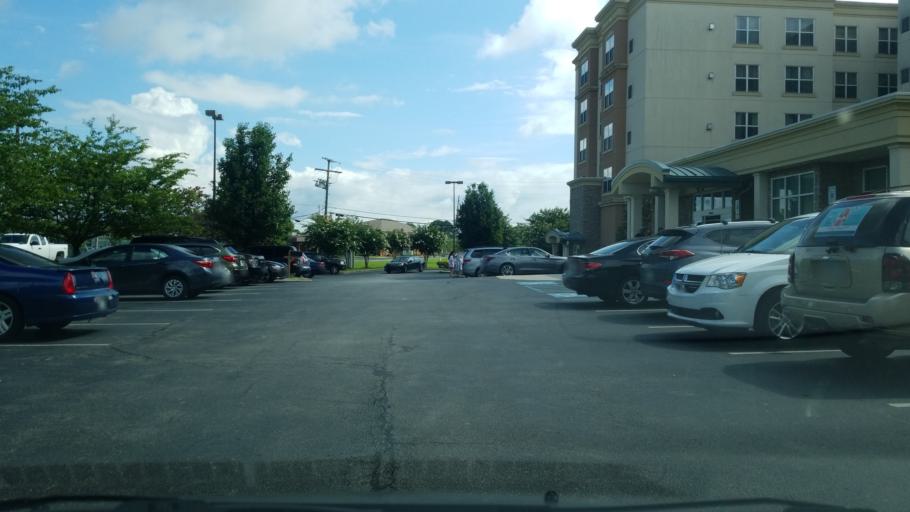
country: US
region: Tennessee
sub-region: Hamilton County
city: East Brainerd
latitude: 35.0466
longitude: -85.1586
